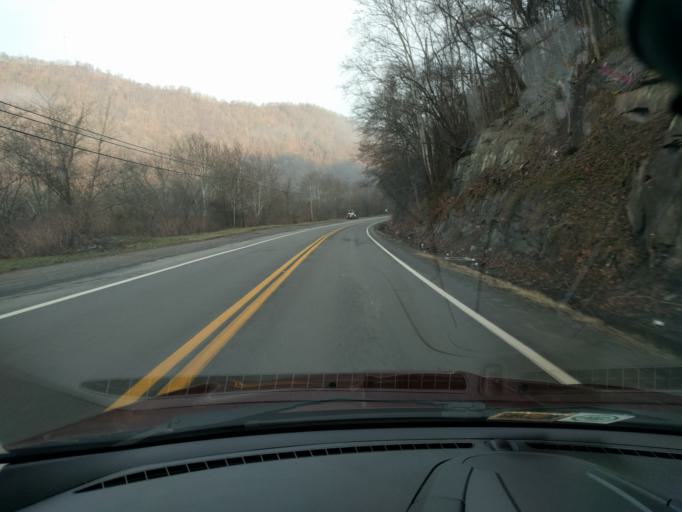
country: US
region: West Virginia
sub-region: Kanawha County
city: Montgomery
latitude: 38.1617
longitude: -81.3000
